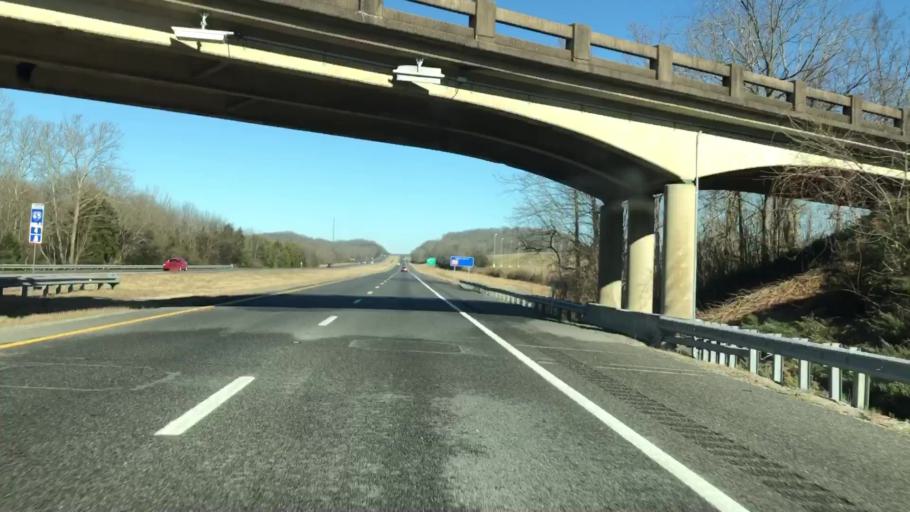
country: US
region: Alabama
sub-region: Limestone County
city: Ardmore
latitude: 35.0622
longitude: -86.8815
